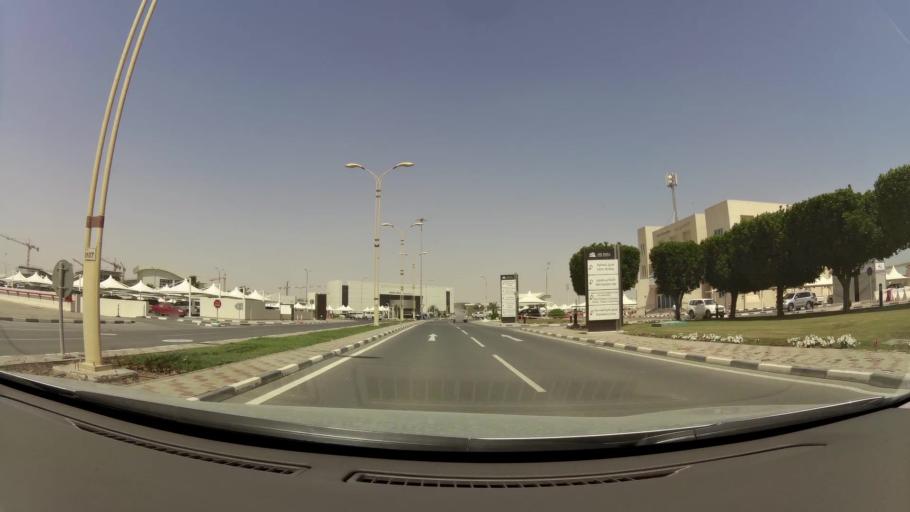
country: QA
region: Baladiyat Umm Salal
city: Umm Salal Muhammad
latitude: 25.3778
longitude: 51.4914
